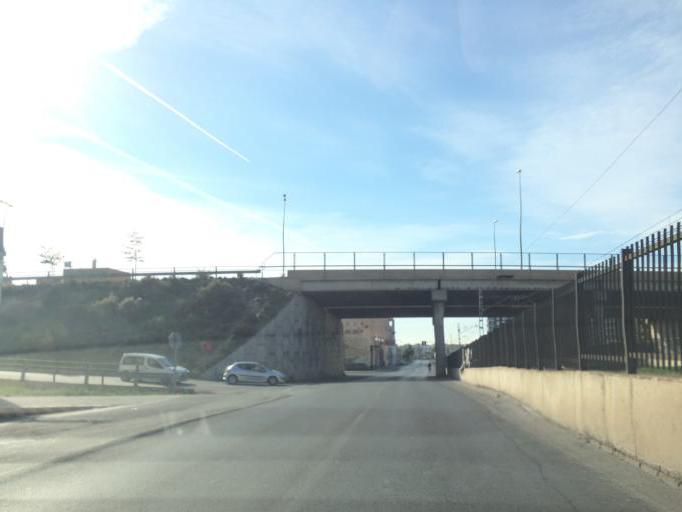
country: ES
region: Andalusia
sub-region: Provincia de Almeria
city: Almeria
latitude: 36.8439
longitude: -2.4378
